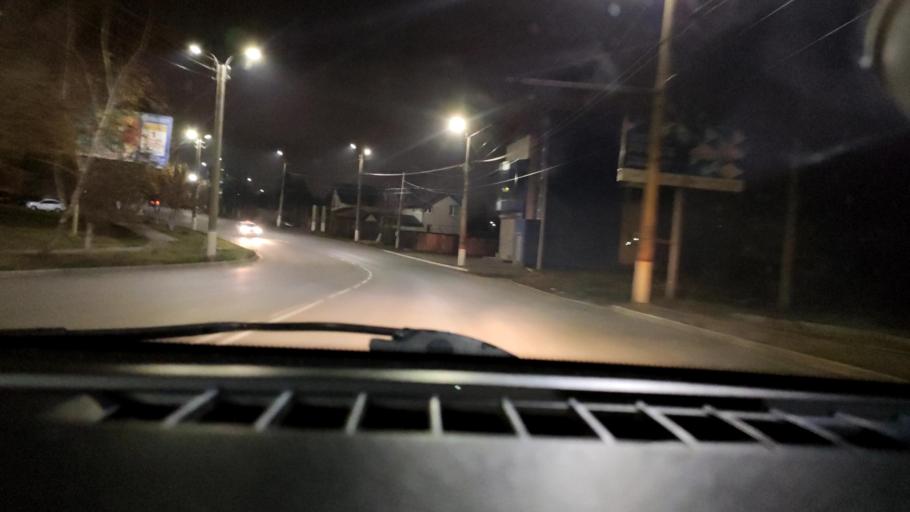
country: RU
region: Samara
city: Novokuybyshevsk
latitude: 53.1090
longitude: 49.9570
